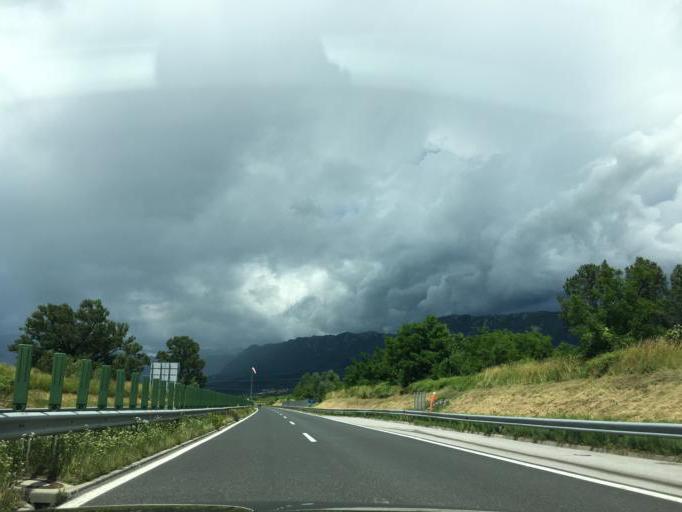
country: SI
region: Vipava
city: Vipava
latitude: 45.8433
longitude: 13.9514
